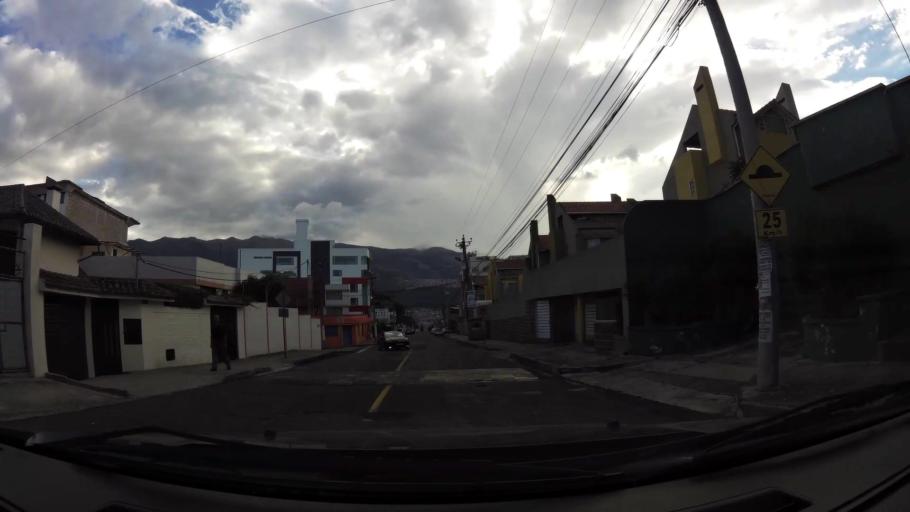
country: EC
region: Pichincha
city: Quito
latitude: -0.1312
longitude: -78.4773
